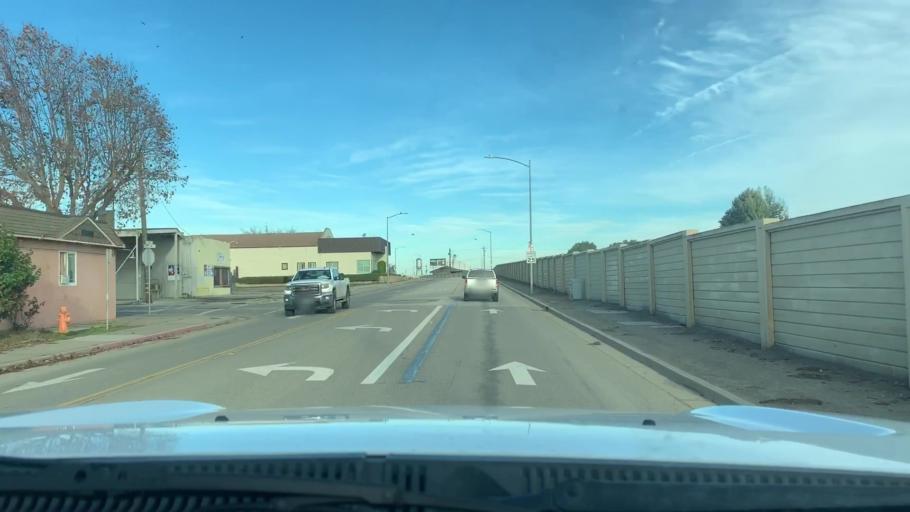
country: US
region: California
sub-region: Monterey County
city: King City
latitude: 36.2103
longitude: -121.1199
